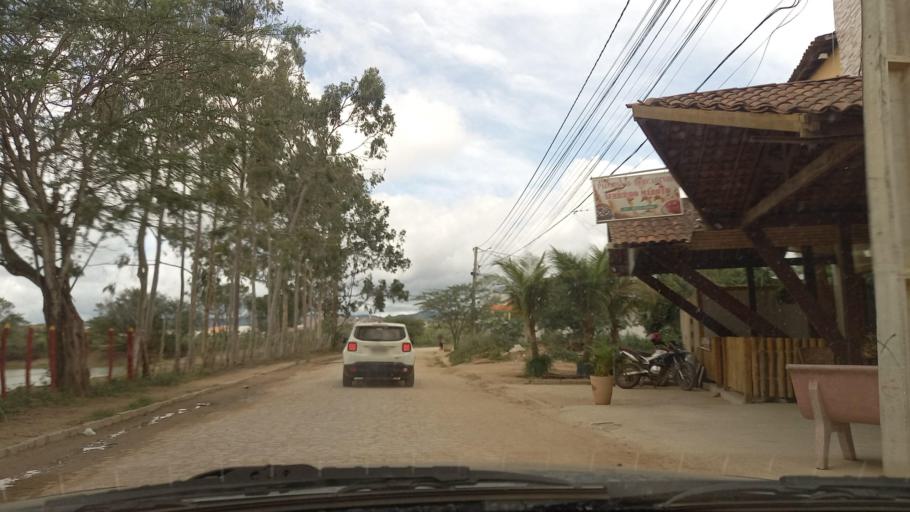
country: BR
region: Pernambuco
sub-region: Gravata
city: Gravata
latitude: -8.1891
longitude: -35.5787
